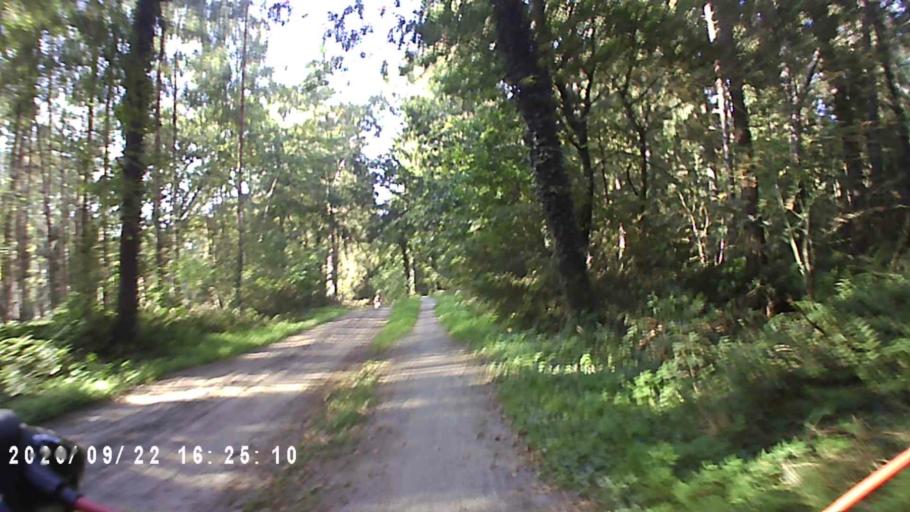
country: NL
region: Groningen
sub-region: Gemeente Leek
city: Leek
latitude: 53.0757
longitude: 6.4397
